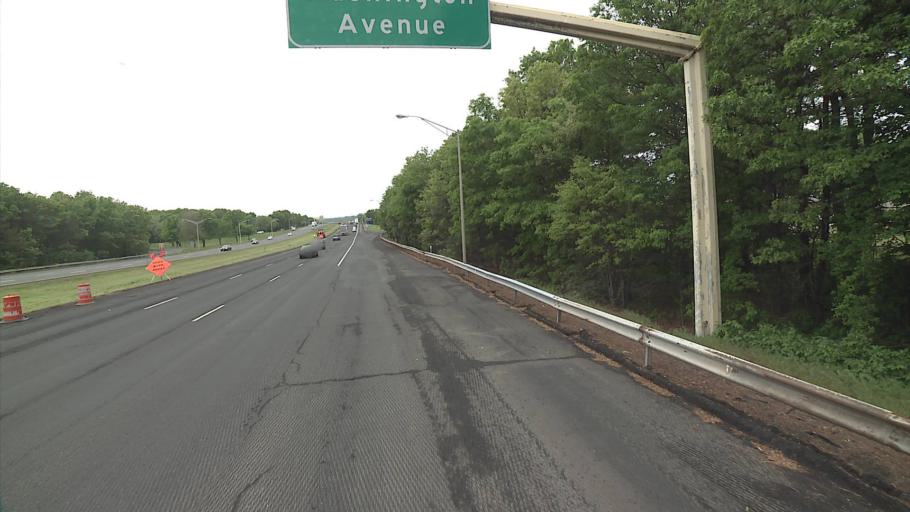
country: US
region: Connecticut
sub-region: New Haven County
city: North Haven
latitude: 41.4005
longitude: -72.8463
